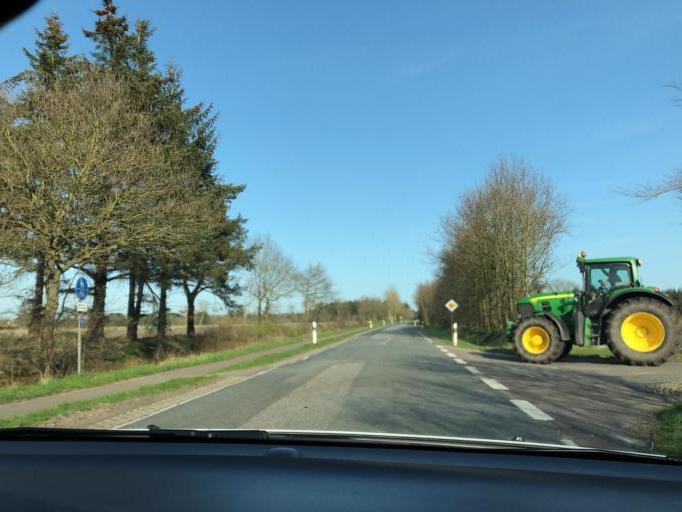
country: DE
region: Schleswig-Holstein
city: Bargum
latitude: 54.6895
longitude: 8.9803
